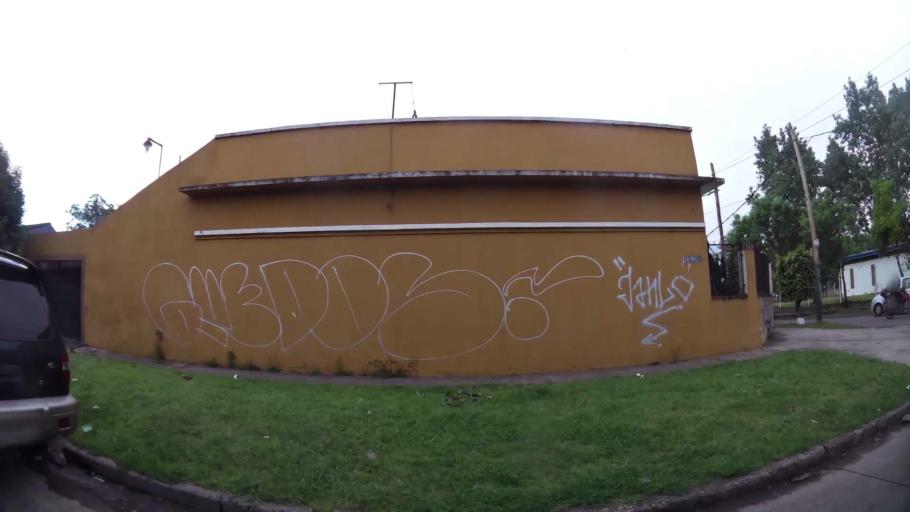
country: AR
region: Buenos Aires
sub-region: Partido de Lomas de Zamora
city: Lomas de Zamora
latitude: -34.7462
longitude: -58.3454
